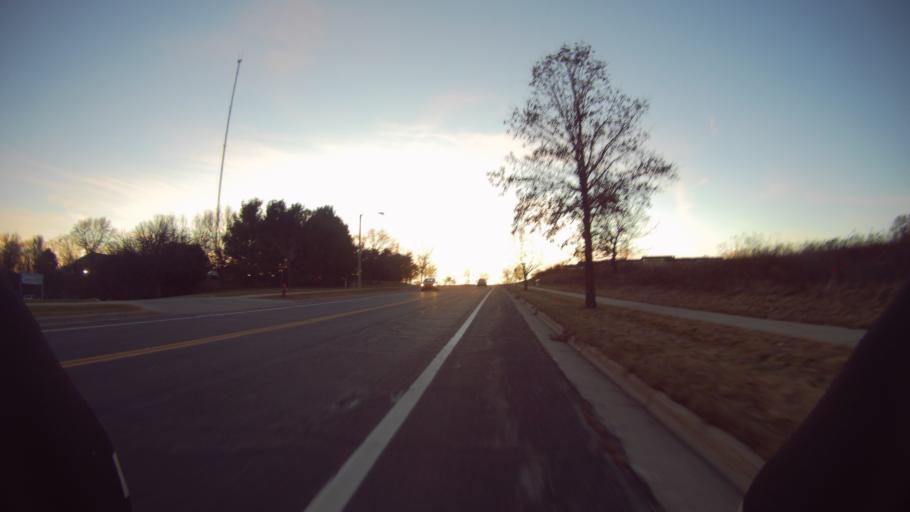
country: US
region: Wisconsin
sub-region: Dane County
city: Shorewood Hills
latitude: 43.0558
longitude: -89.4824
